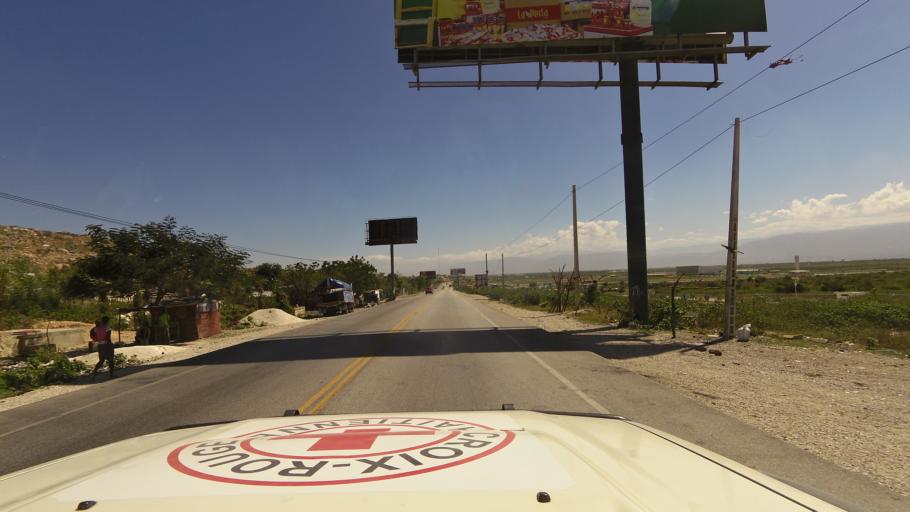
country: HT
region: Ouest
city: Croix des Bouquets
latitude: 18.6620
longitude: -72.2944
